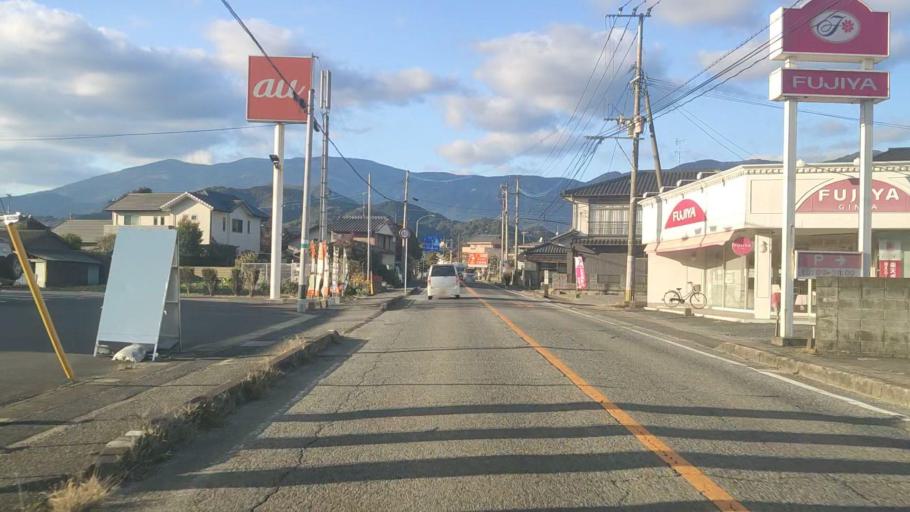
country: JP
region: Saga Prefecture
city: Saga-shi
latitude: 33.2917
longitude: 130.2035
